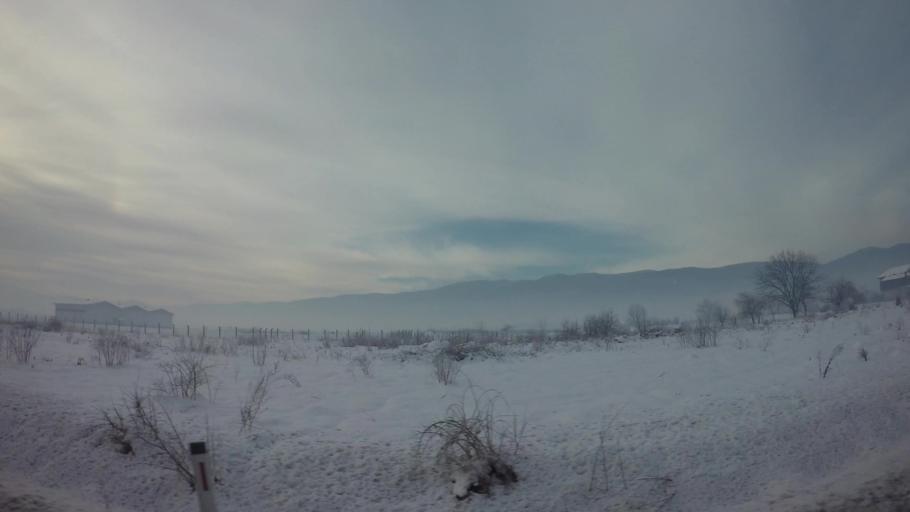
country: BA
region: Federation of Bosnia and Herzegovina
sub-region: Kanton Sarajevo
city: Sarajevo
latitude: 43.8248
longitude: 18.3448
